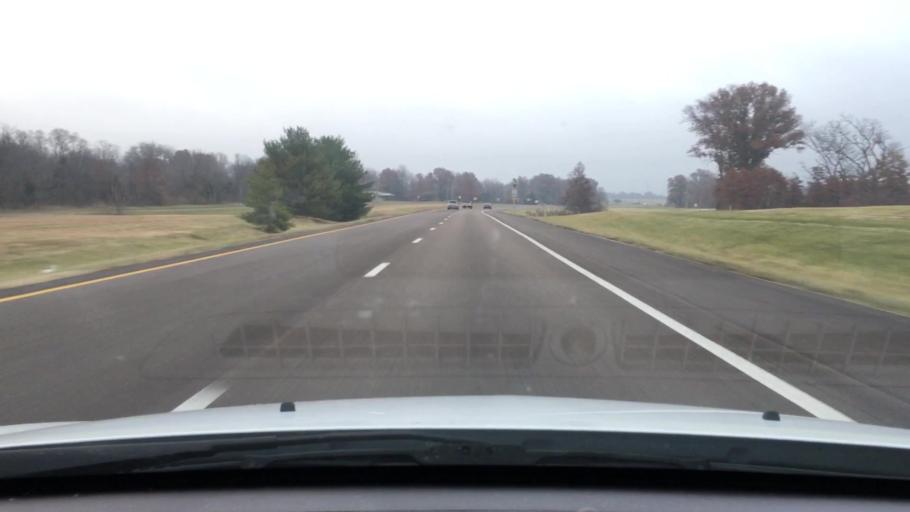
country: US
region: Missouri
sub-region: Callaway County
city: Fulton
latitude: 38.9562
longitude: -91.9340
